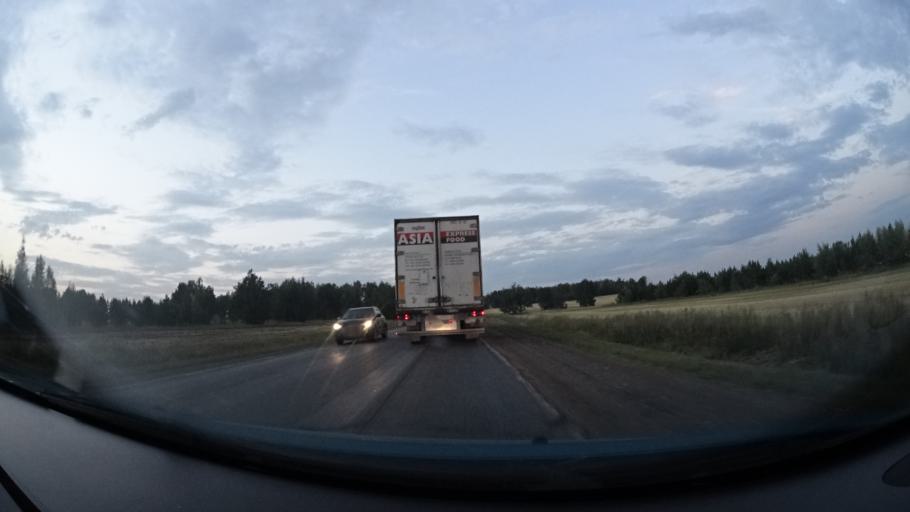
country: RU
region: Tatarstan
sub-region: Bavlinskiy Rayon
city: Bavly
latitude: 54.2847
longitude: 52.9944
